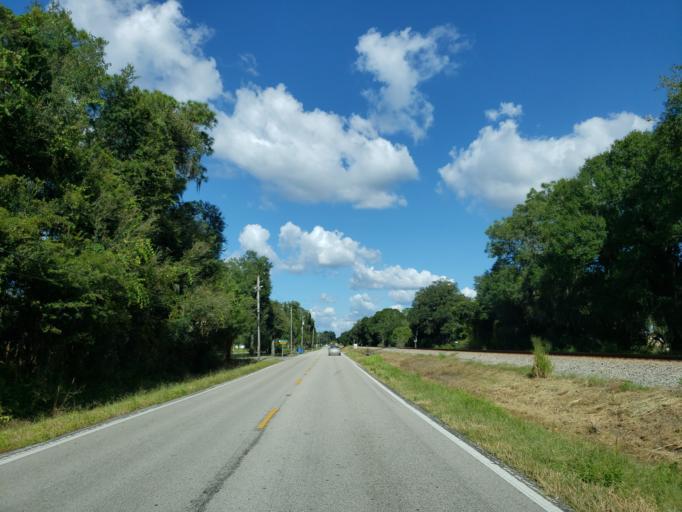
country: US
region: Florida
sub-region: Hillsborough County
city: Dover
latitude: 27.9739
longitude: -82.1911
